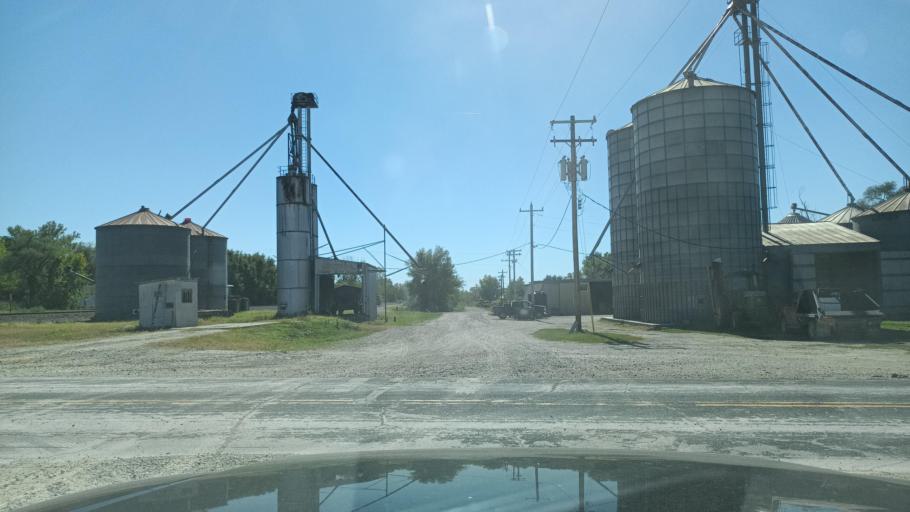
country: US
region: Missouri
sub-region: Macon County
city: La Plata
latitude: 39.9573
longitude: -92.6508
